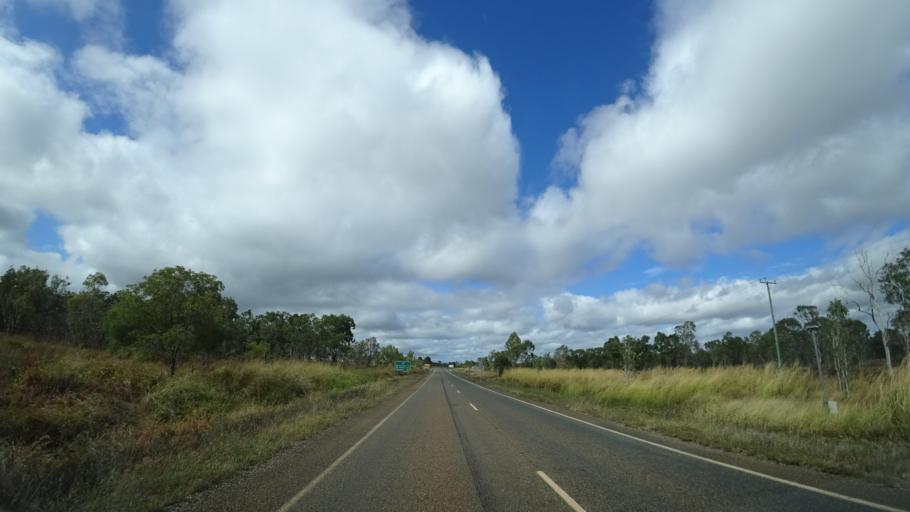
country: AU
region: Queensland
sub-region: Cook
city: Cooktown
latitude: -15.8653
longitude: 144.8588
